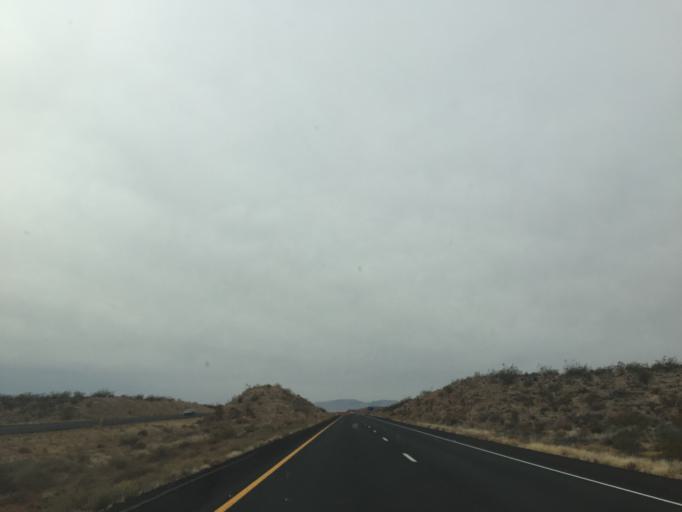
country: US
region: Utah
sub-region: Washington County
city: Washington
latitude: 37.1769
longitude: -113.4257
